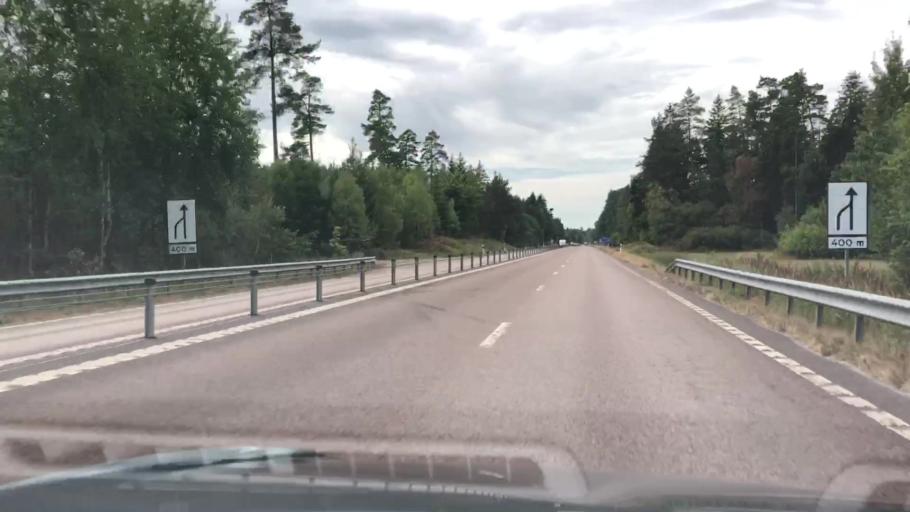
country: SE
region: Kalmar
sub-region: Torsas Kommun
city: Torsas
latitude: 56.2858
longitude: 15.9832
